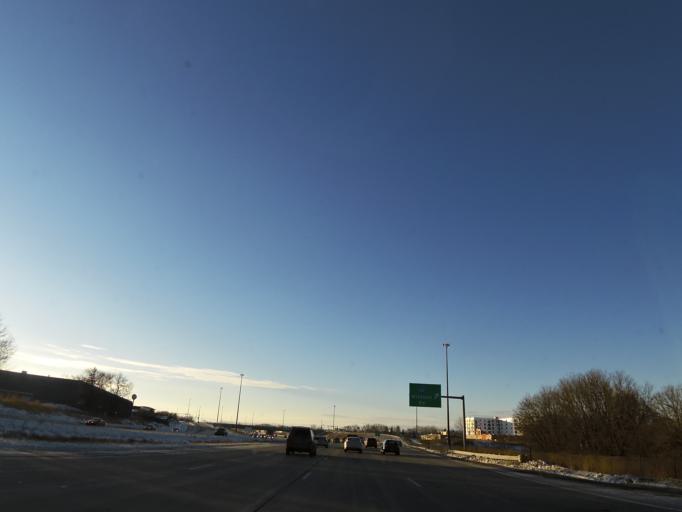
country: US
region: Minnesota
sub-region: Hennepin County
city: Eden Prairie
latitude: 44.8613
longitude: -93.4536
